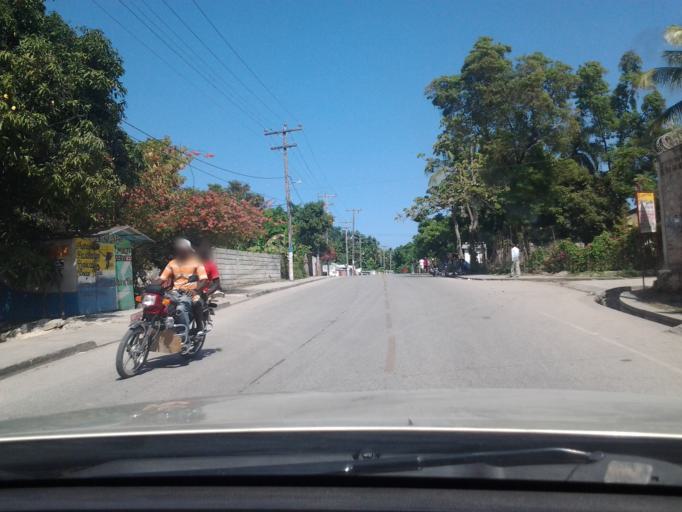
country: HT
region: Ouest
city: Tigwav
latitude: 18.4350
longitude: -72.8596
